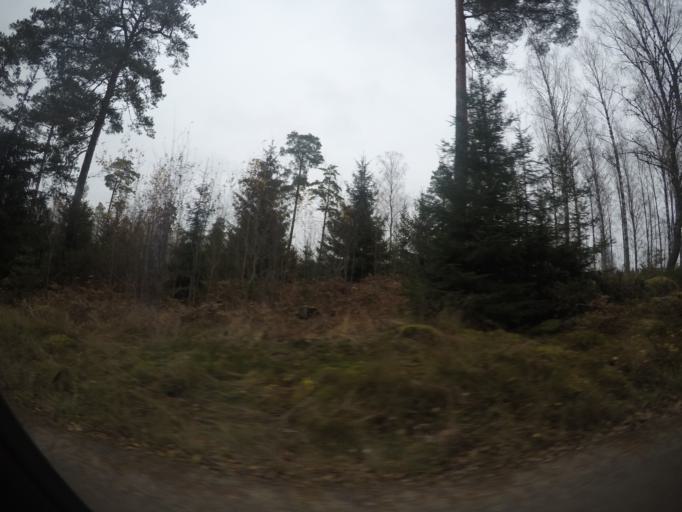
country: SE
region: Vaestmanland
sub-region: Kopings Kommun
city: Koping
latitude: 59.5911
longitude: 16.0859
